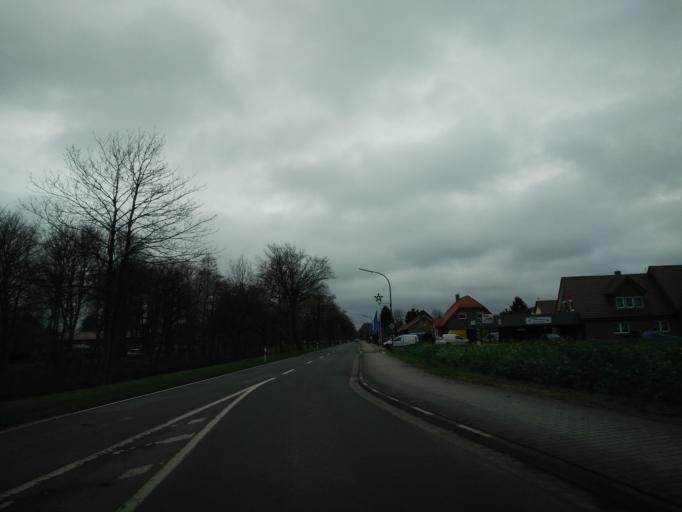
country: NL
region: Drenthe
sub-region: Gemeente Emmen
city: Emmer-Compascuum
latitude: 52.7821
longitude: 7.1076
